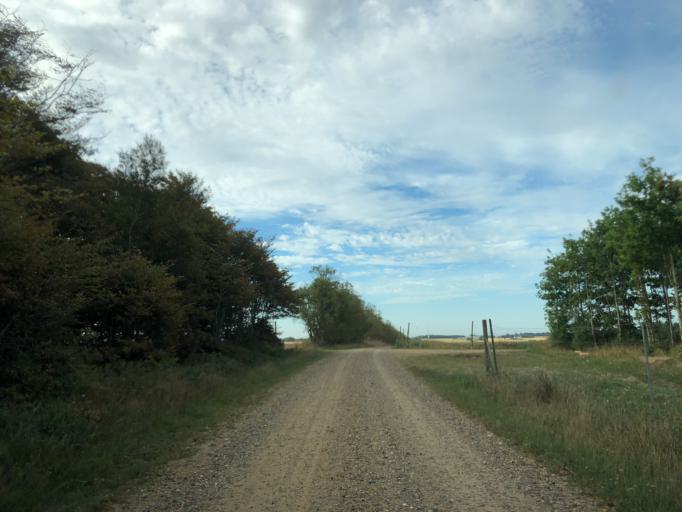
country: DK
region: Central Jutland
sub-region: Ringkobing-Skjern Kommune
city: Skjern
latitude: 56.0777
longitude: 8.4233
